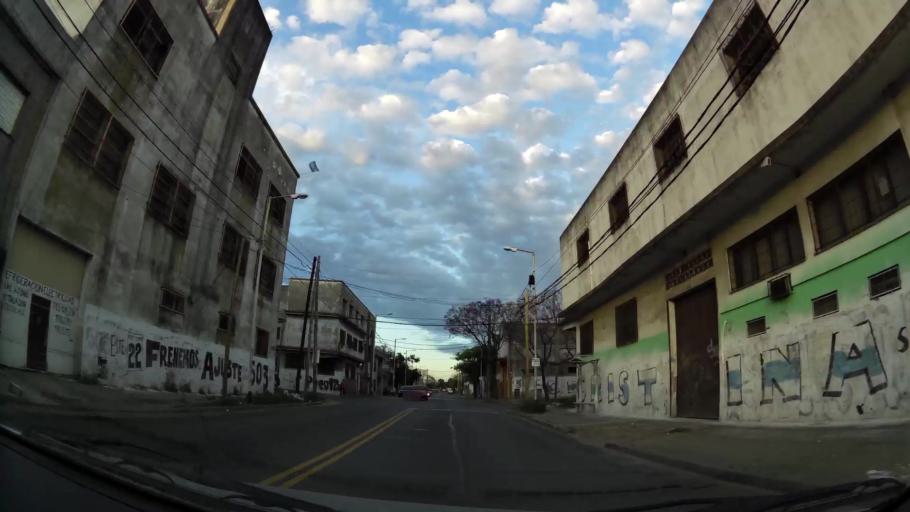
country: AR
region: Buenos Aires
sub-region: Partido de Avellaneda
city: Avellaneda
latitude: -34.7008
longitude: -58.3307
